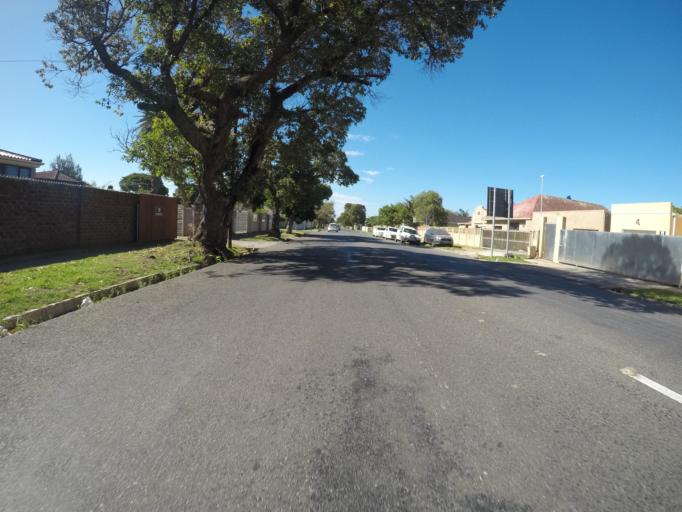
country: ZA
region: Eastern Cape
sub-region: Buffalo City Metropolitan Municipality
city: East London
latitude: -32.9824
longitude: 27.9110
